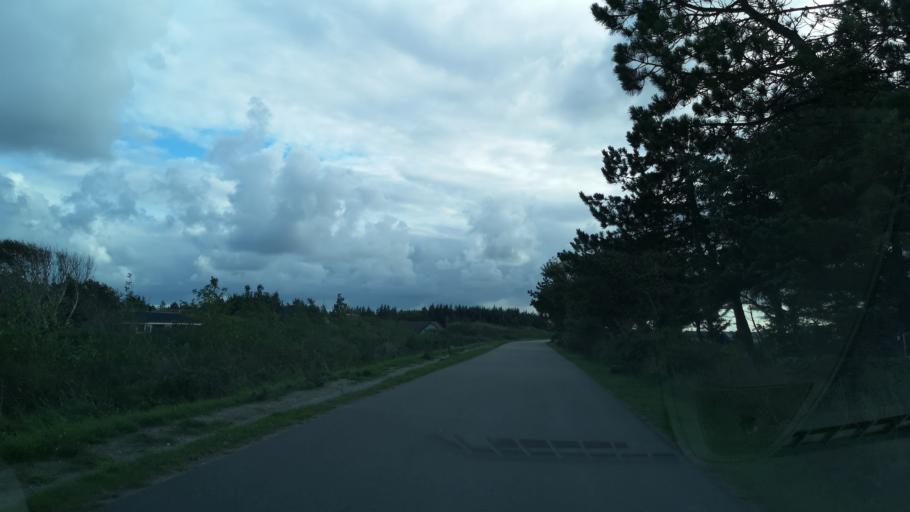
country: DK
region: Central Jutland
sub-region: Ringkobing-Skjern Kommune
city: Ringkobing
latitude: 56.1303
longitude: 8.1315
